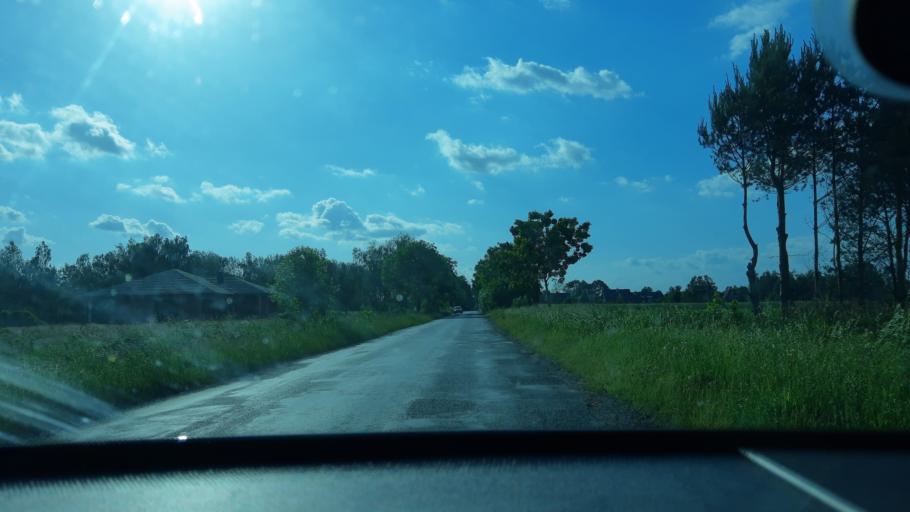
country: PL
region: Lodz Voivodeship
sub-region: Powiat sieradzki
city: Sieradz
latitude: 51.5443
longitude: 18.7869
